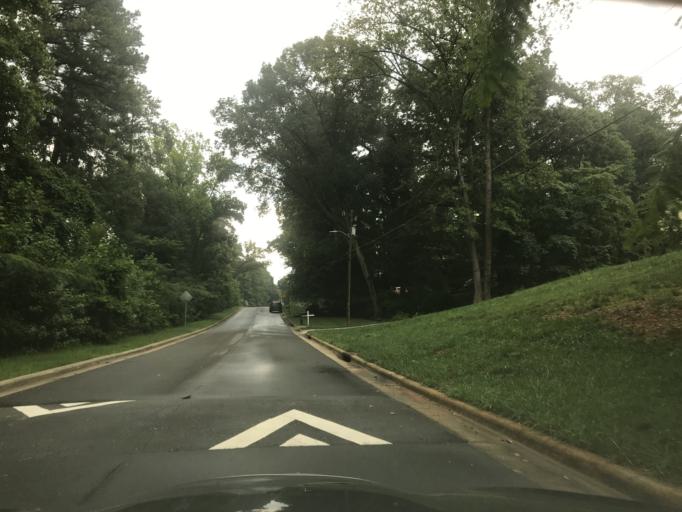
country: US
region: North Carolina
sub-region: Wake County
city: West Raleigh
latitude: 35.8353
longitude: -78.6617
